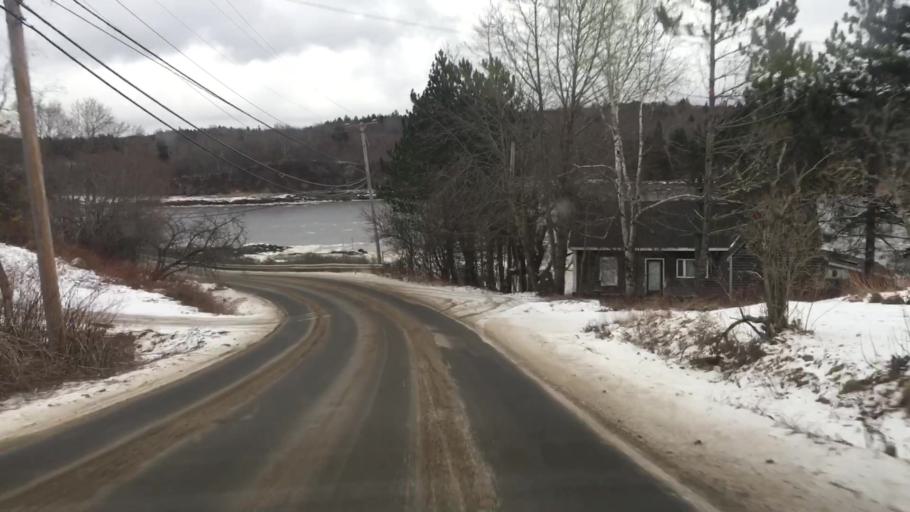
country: US
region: Maine
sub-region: Washington County
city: Machiasport
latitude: 44.6958
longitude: -67.3952
